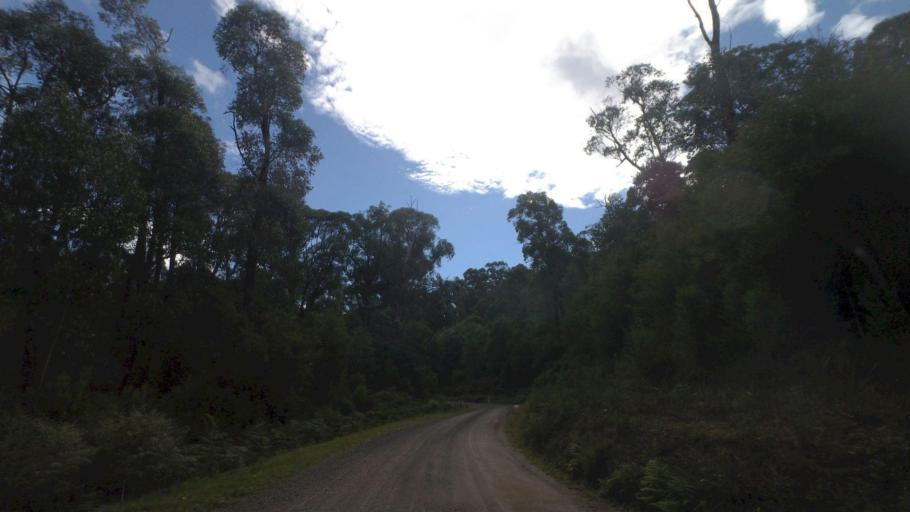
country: AU
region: Victoria
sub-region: Cardinia
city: Bunyip
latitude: -37.9902
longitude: 145.8145
